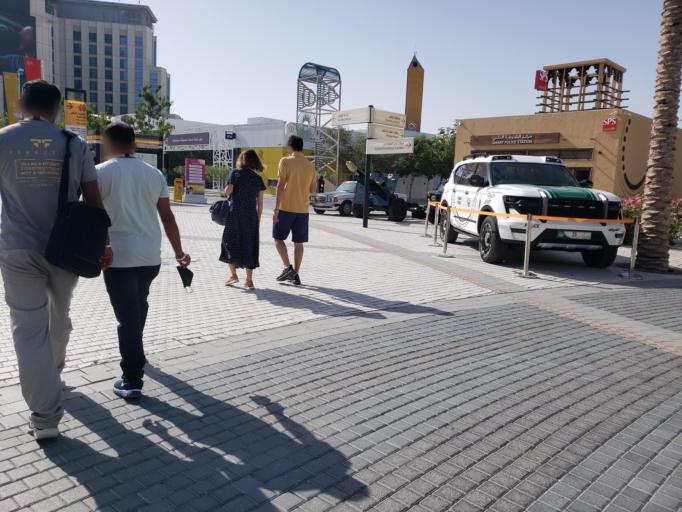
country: AE
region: Dubai
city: Dubai
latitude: 24.9620
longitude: 55.1486
